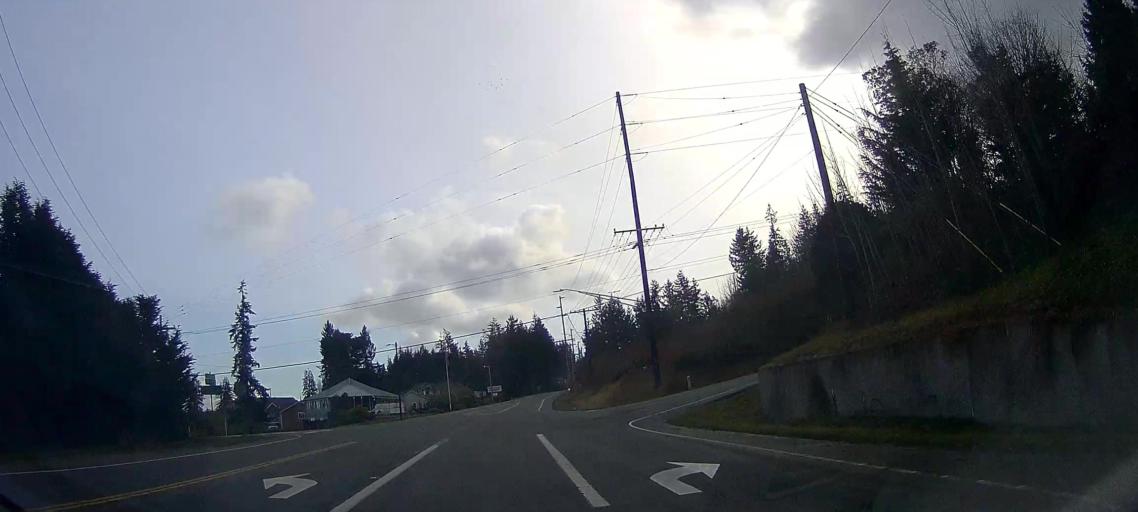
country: US
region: Washington
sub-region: Island County
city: Camano
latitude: 48.1649
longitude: -122.4793
